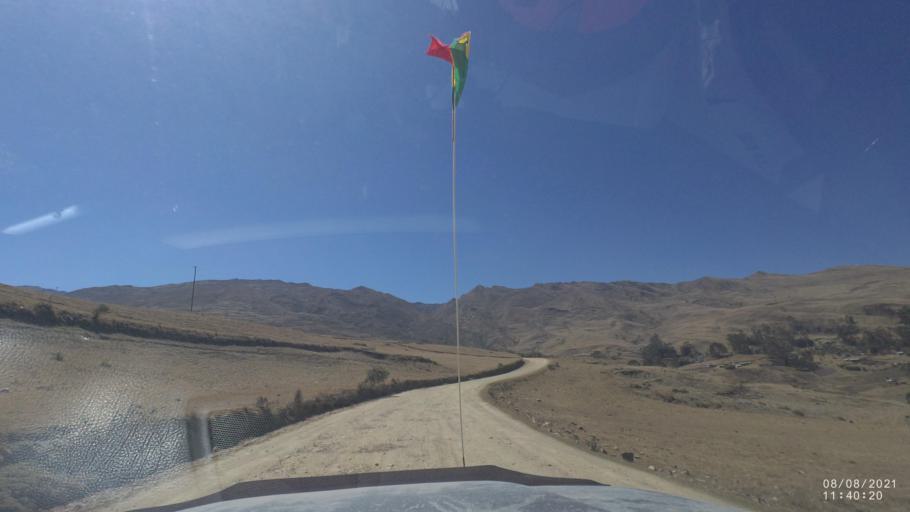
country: BO
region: Cochabamba
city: Colchani
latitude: -16.7970
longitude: -66.6488
